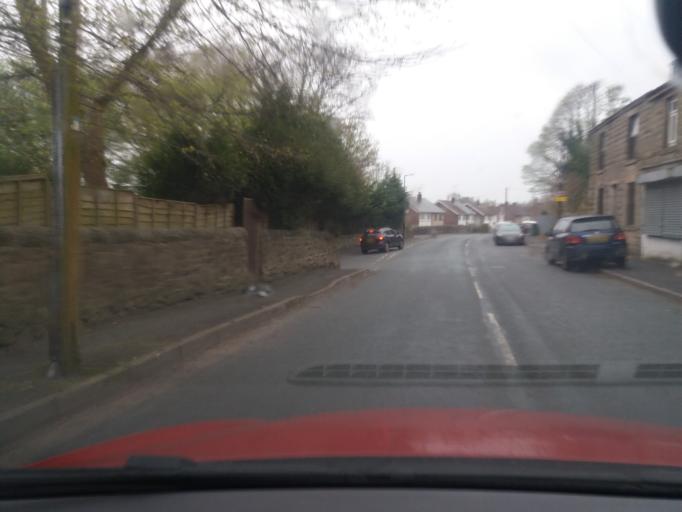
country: GB
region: England
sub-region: Lancashire
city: Clayton-le-Woods
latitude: 53.6896
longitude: -2.6366
